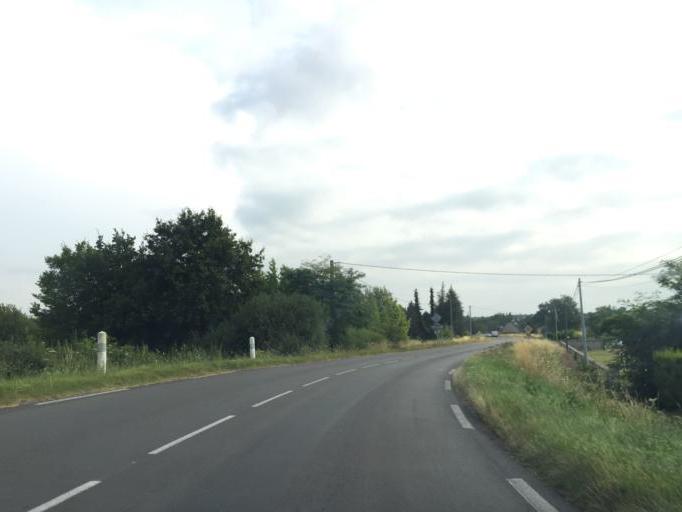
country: FR
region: Auvergne
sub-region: Departement de l'Allier
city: Molinet
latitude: 46.4634
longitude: 3.9345
